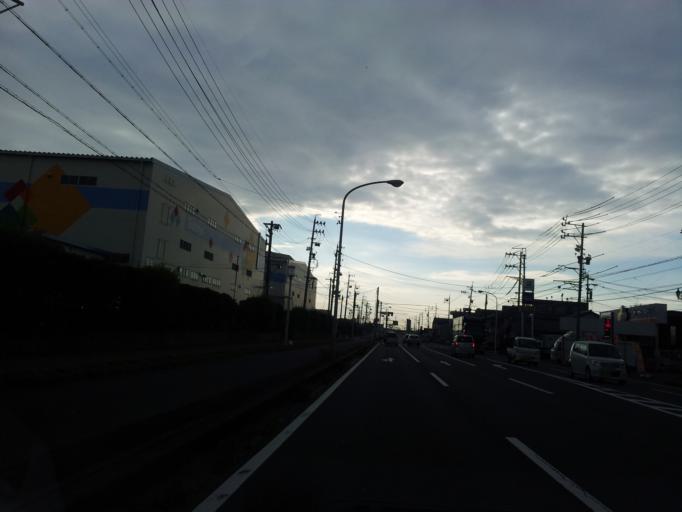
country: JP
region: Shizuoka
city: Shizuoka-shi
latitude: 34.9903
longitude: 138.4968
